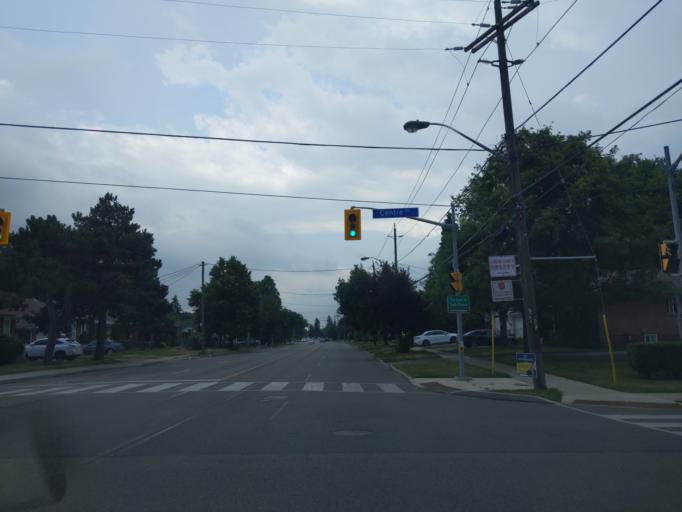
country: CA
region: Ontario
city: North York
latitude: 43.7931
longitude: -79.4120
